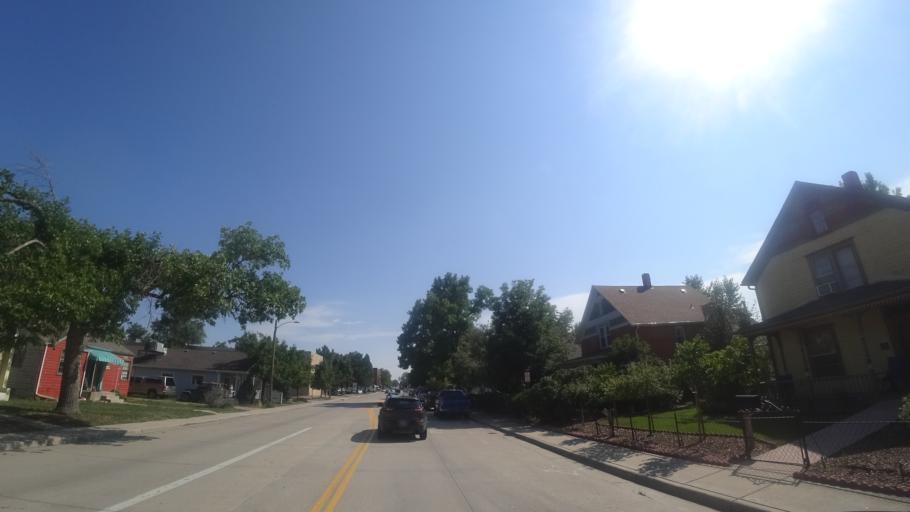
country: US
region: Colorado
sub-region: Arapahoe County
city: Littleton
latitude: 39.6168
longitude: -105.0162
